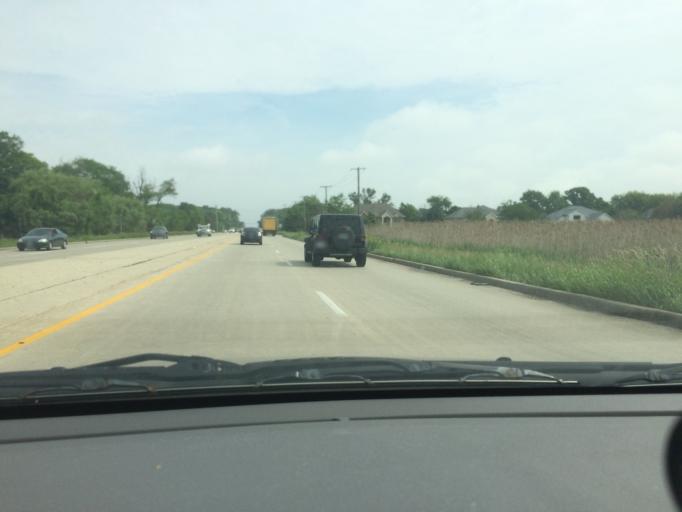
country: US
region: Illinois
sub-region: Cook County
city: Bartlett
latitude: 41.9797
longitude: -88.2073
